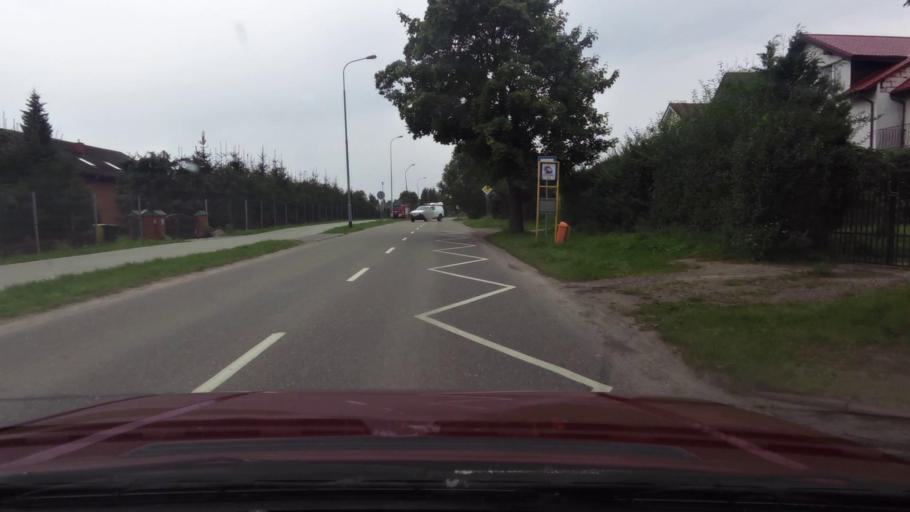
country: PL
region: West Pomeranian Voivodeship
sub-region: Powiat kolobrzeski
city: Kolobrzeg
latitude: 54.1544
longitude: 15.5421
